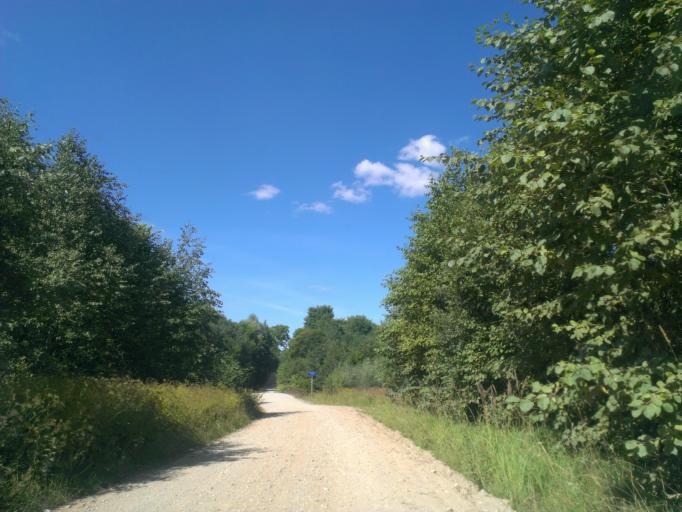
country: LV
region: Malpils
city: Malpils
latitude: 57.0116
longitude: 24.9902
